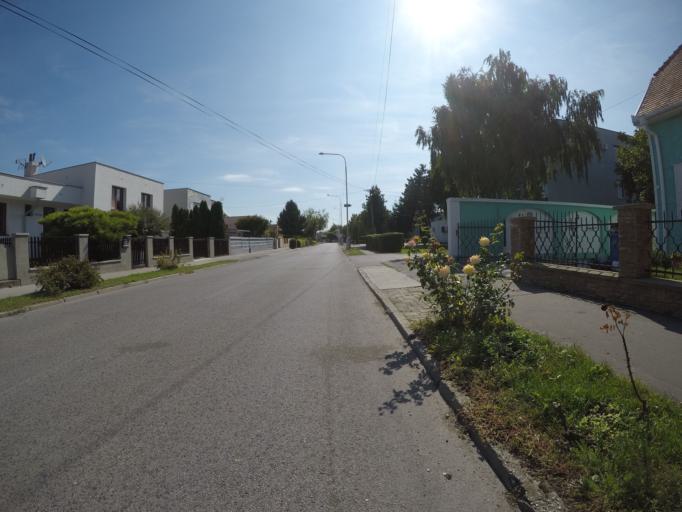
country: SK
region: Trnavsky
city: Dunajska Streda
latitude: 47.9888
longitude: 17.6084
